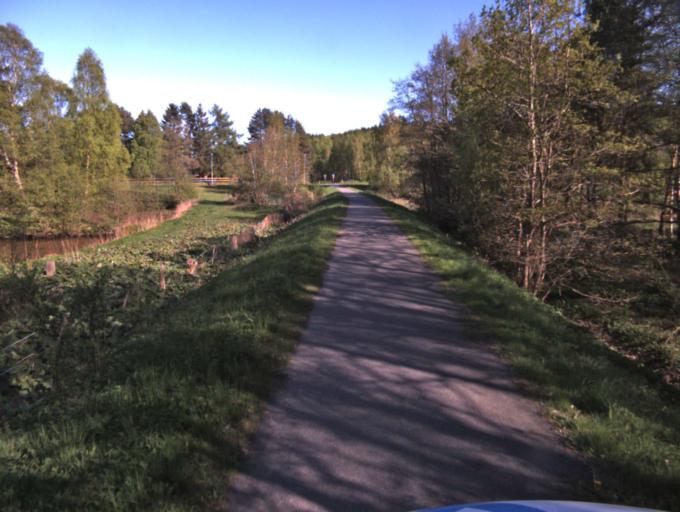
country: SE
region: Skane
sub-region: Kristianstads Kommun
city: Degeberga
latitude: 55.8269
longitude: 14.0936
